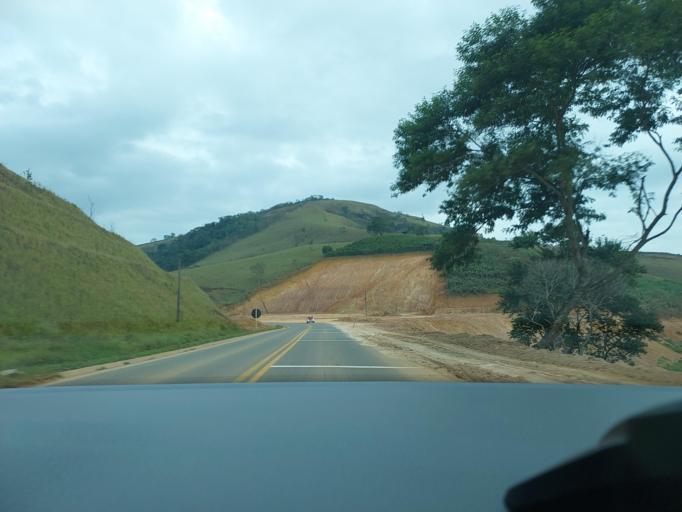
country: BR
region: Minas Gerais
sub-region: Mirai
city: Mirai
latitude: -20.9859
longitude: -42.5796
